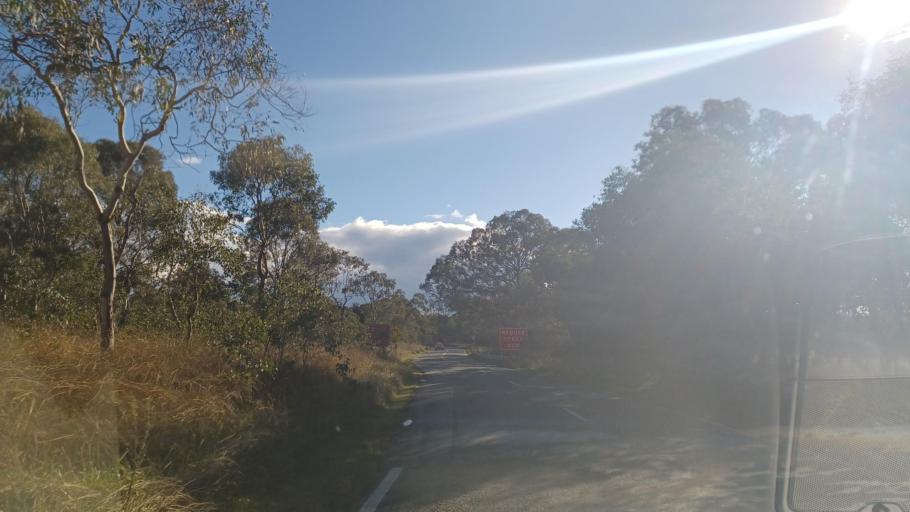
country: AU
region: Australian Capital Territory
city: Belconnen
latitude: -35.1879
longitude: 149.0502
